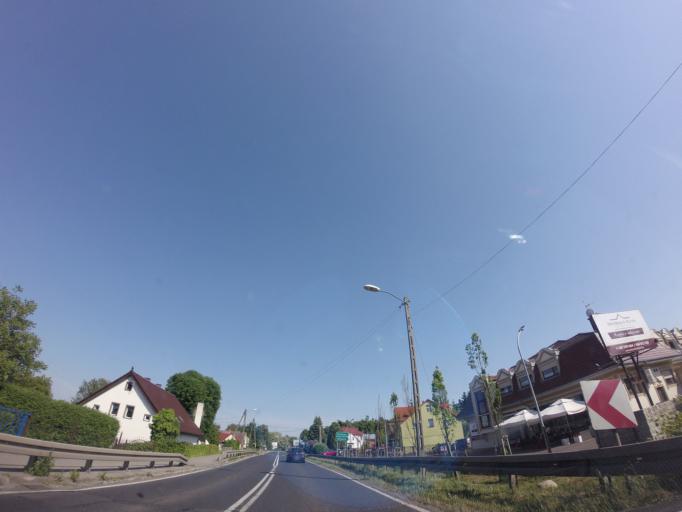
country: PL
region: West Pomeranian Voivodeship
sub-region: Powiat gryfinski
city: Stare Czarnowo
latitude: 53.3439
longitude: 14.7525
